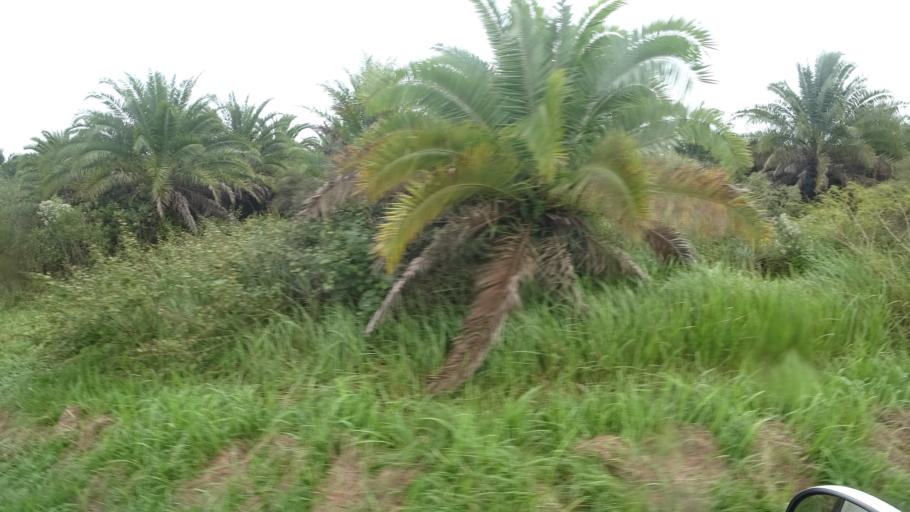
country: US
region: Florida
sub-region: Sarasota County
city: Warm Mineral Springs
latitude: 27.2834
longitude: -82.1754
